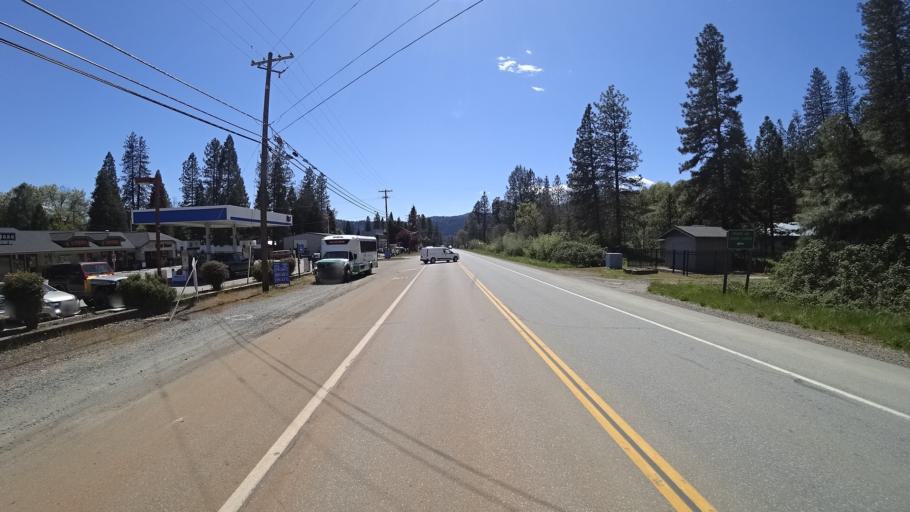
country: US
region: California
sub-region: Trinity County
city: Weaverville
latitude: 40.7378
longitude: -122.9286
